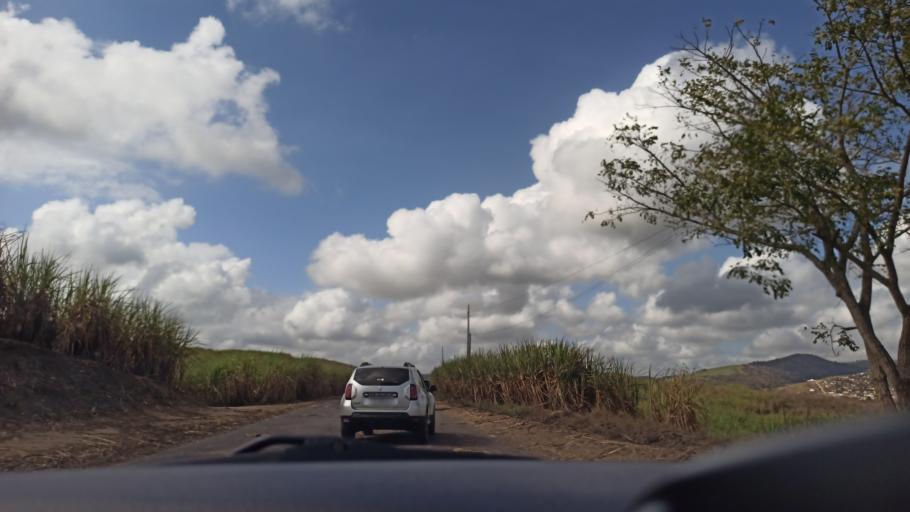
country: BR
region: Paraiba
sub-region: Juripiranga
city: Juripiranga
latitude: -7.4026
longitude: -35.2582
